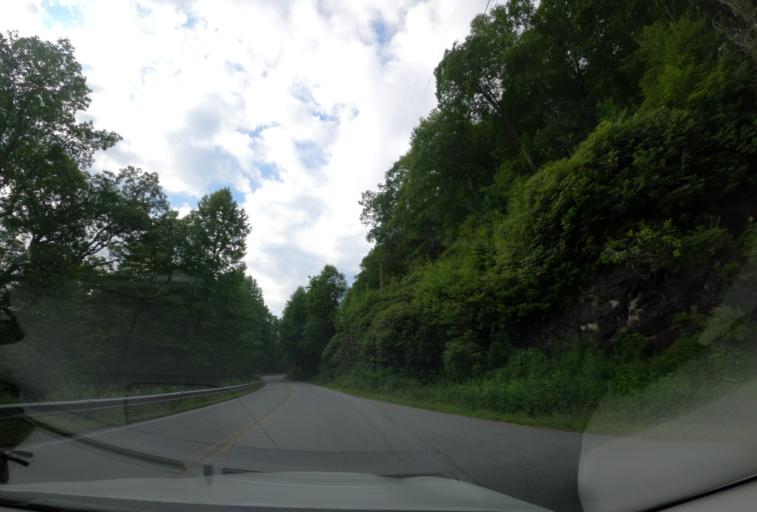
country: US
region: North Carolina
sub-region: Jackson County
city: Cullowhee
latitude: 35.0983
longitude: -83.1503
